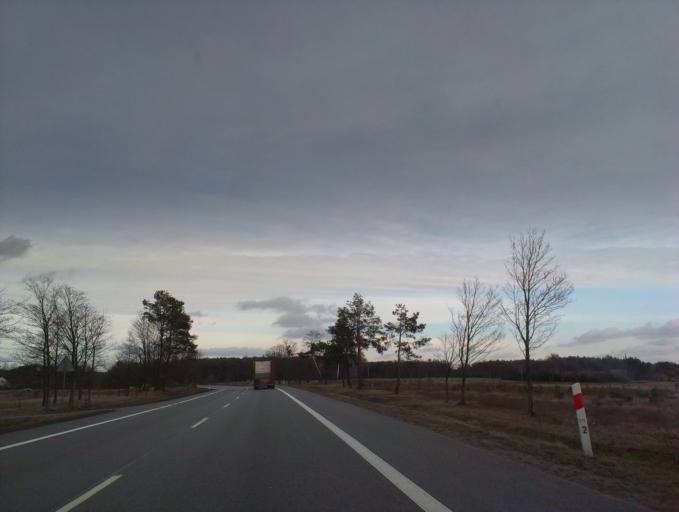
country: PL
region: Kujawsko-Pomorskie
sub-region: Powiat lipnowski
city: Skepe
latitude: 52.8933
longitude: 19.4372
